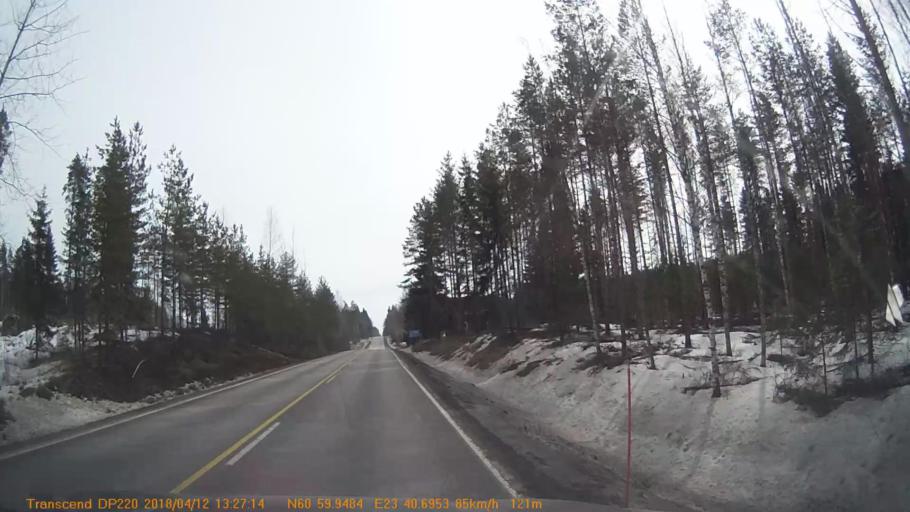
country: FI
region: Pirkanmaa
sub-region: Etelae-Pirkanmaa
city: Kylmaekoski
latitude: 60.9989
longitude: 23.6785
